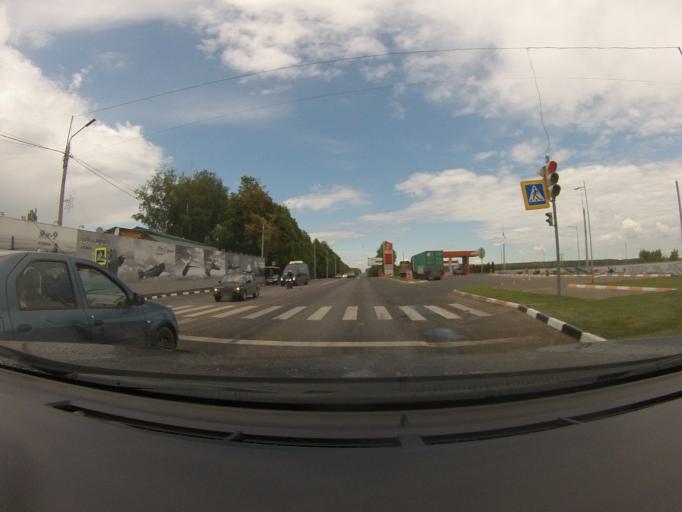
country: RU
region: Tula
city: Gorelki
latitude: 54.2645
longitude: 37.6013
